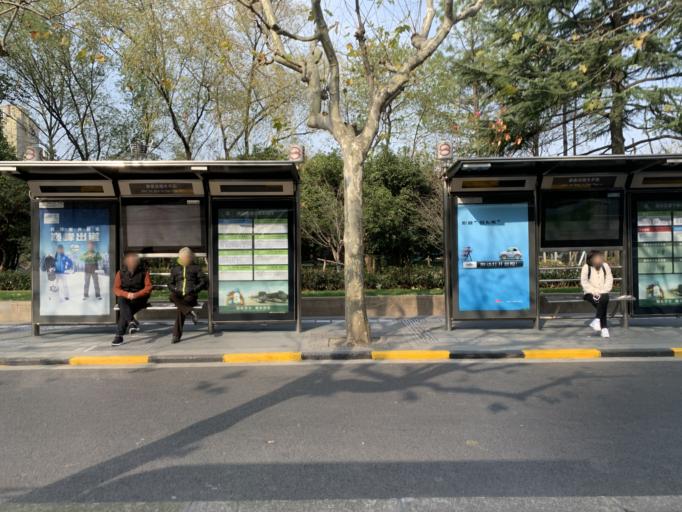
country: CN
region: Shanghai Shi
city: Xuhui
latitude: 31.1983
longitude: 121.4381
